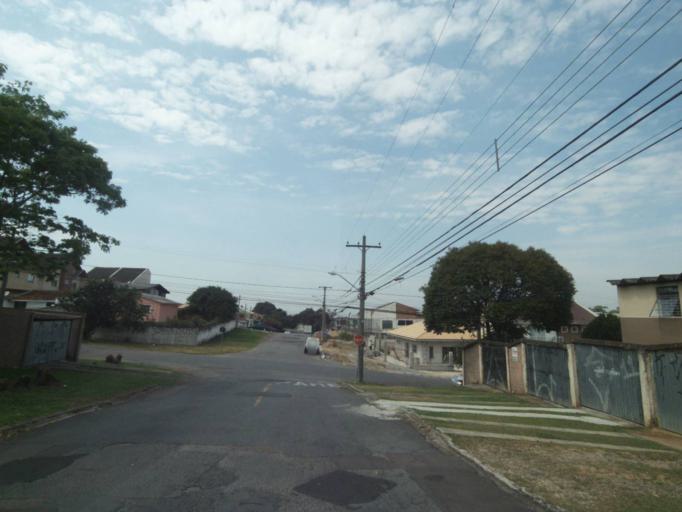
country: BR
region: Parana
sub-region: Pinhais
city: Pinhais
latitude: -25.4004
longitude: -49.2081
